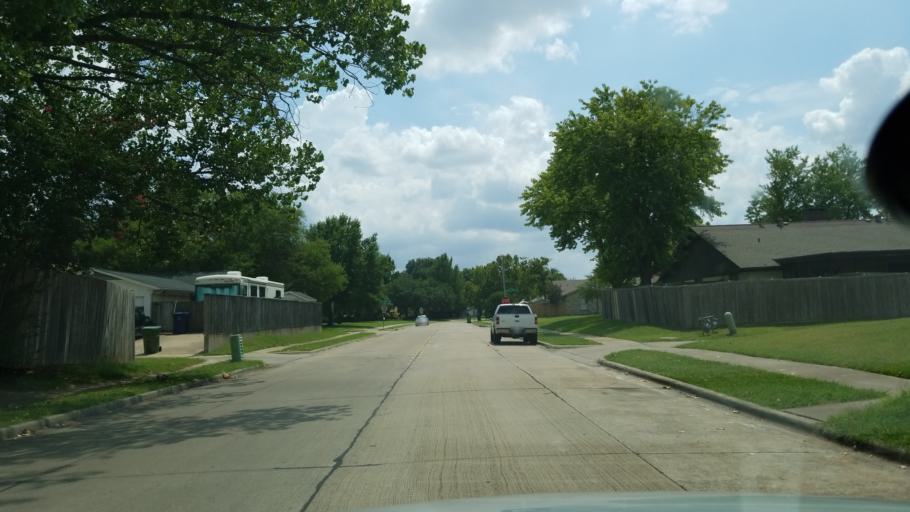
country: US
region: Texas
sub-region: Dallas County
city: Garland
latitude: 32.9249
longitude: -96.6574
